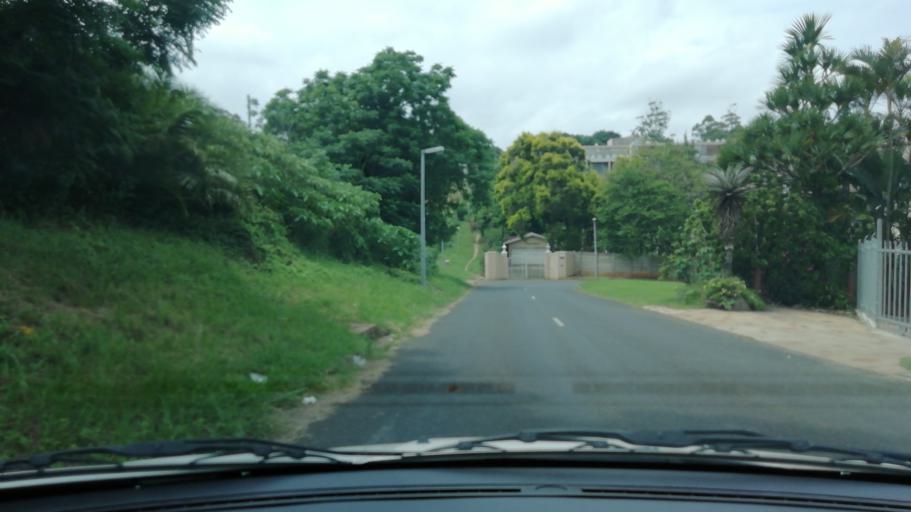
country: ZA
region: KwaZulu-Natal
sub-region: uThungulu District Municipality
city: Empangeni
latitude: -28.7491
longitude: 31.8866
